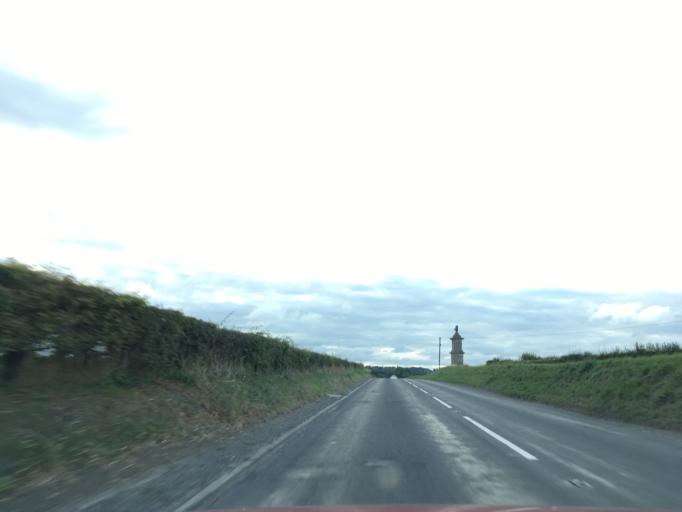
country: GB
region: England
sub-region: Wiltshire
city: Devizes
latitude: 51.3369
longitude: -1.9575
